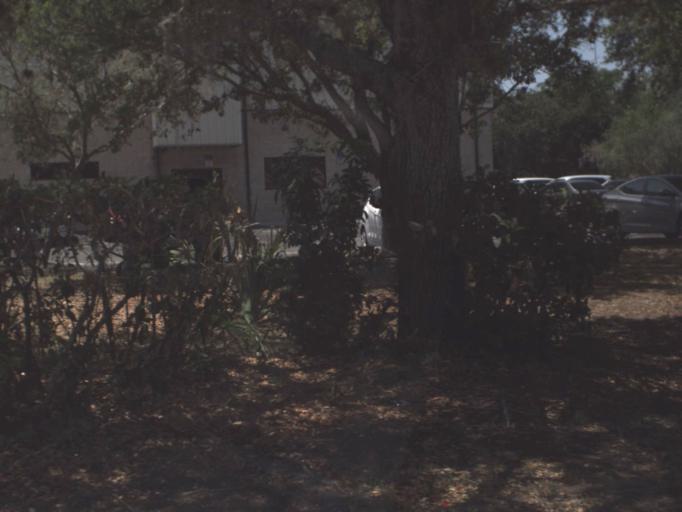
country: US
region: Florida
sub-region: Orange County
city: Orlando
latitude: 28.5476
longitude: -81.4121
